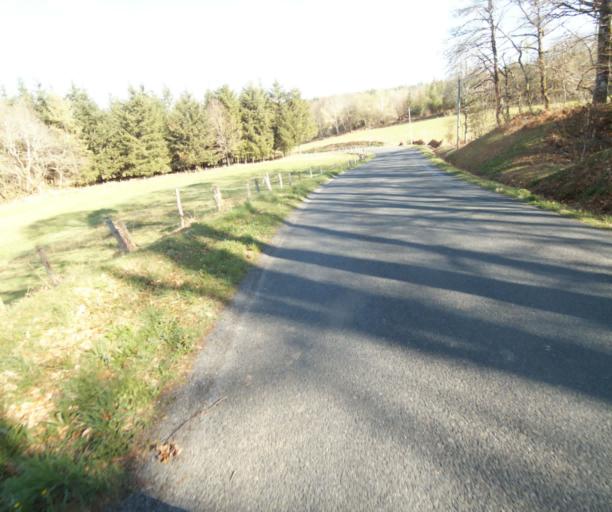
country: FR
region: Limousin
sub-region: Departement de la Correze
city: Correze
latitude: 45.2845
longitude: 1.8750
